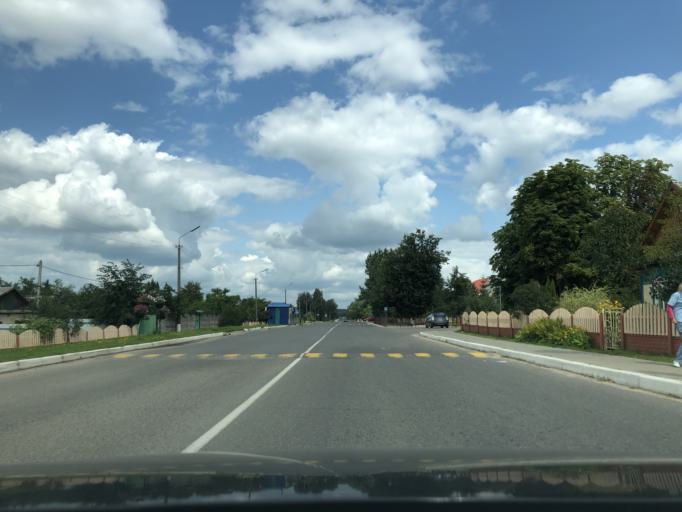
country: BY
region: Minsk
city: Lahoysk
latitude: 54.2102
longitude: 27.8519
